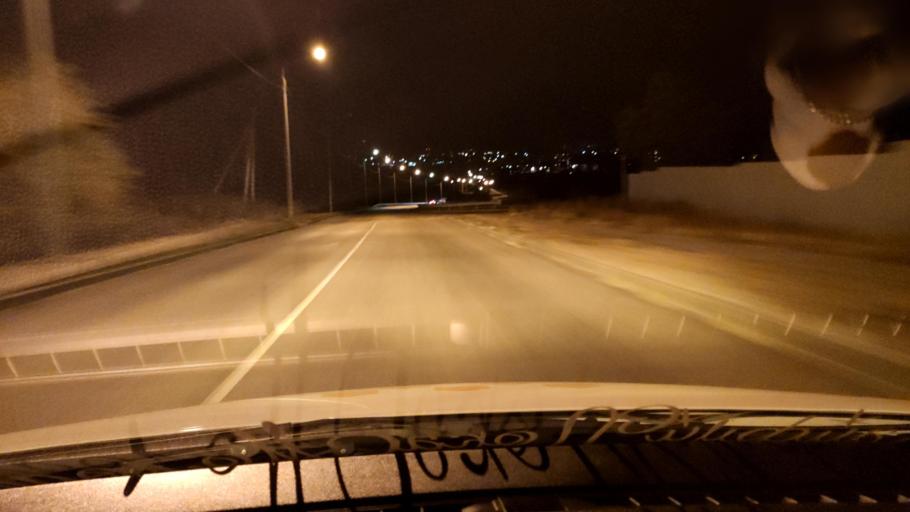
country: RU
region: Voronezj
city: Semiluki
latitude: 51.6705
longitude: 39.0366
